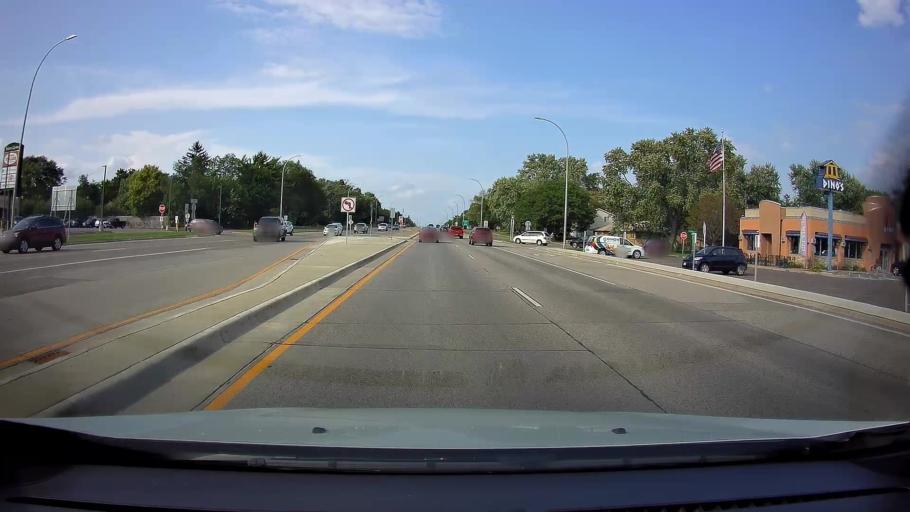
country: US
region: Minnesota
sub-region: Ramsey County
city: Falcon Heights
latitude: 44.9922
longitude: -93.1666
